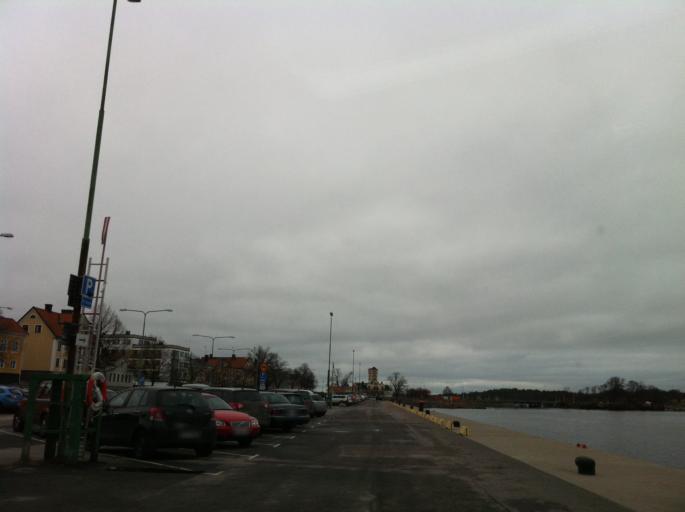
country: SE
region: Kalmar
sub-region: Vasterviks Kommun
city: Vaestervik
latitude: 57.7962
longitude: 16.6211
